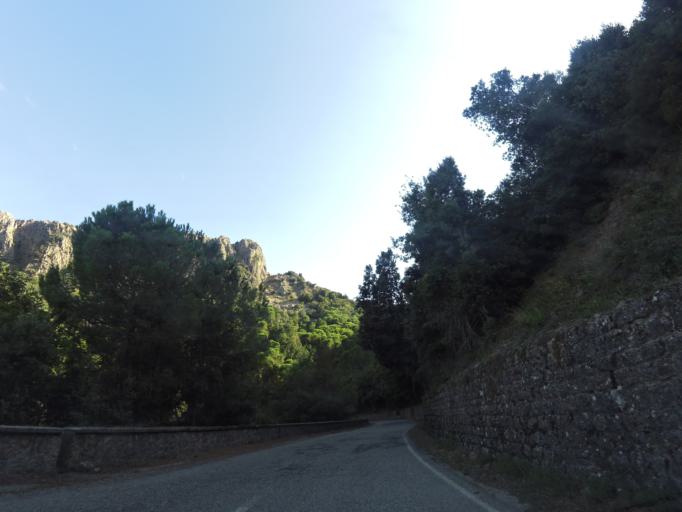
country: IT
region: Calabria
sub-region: Provincia di Reggio Calabria
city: Pazzano
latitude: 38.4644
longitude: 16.4235
